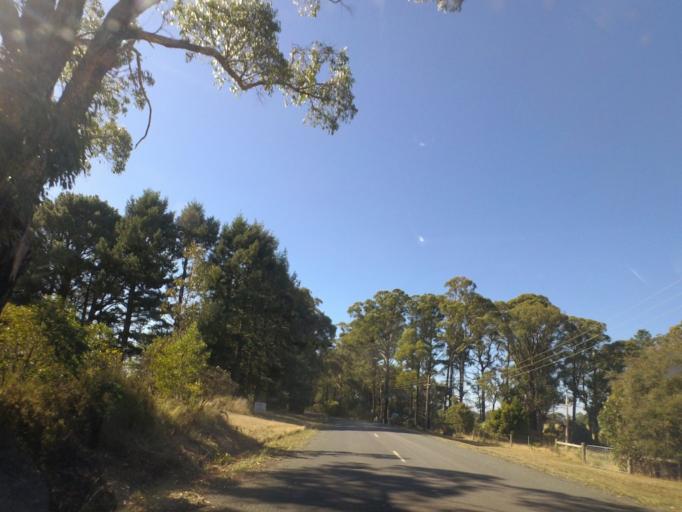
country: AU
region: Victoria
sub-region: Murrindindi
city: Kinglake West
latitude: -37.4767
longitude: 145.3260
